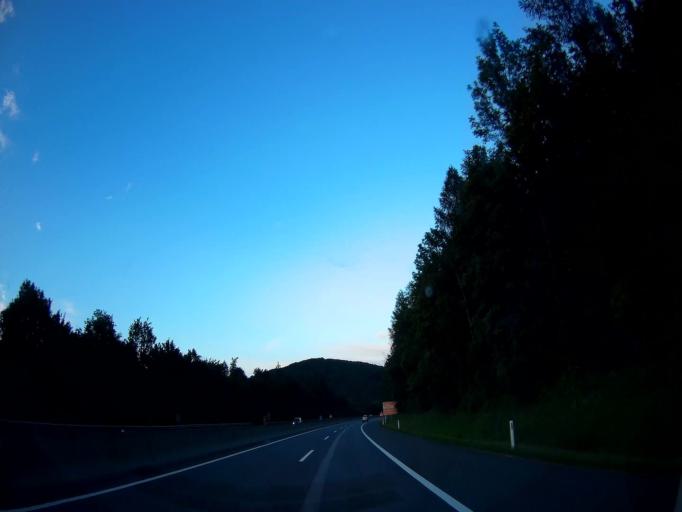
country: AT
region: Lower Austria
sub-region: Politischer Bezirk Wien-Umgebung
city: Wolfsgraben
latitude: 48.1752
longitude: 16.1131
